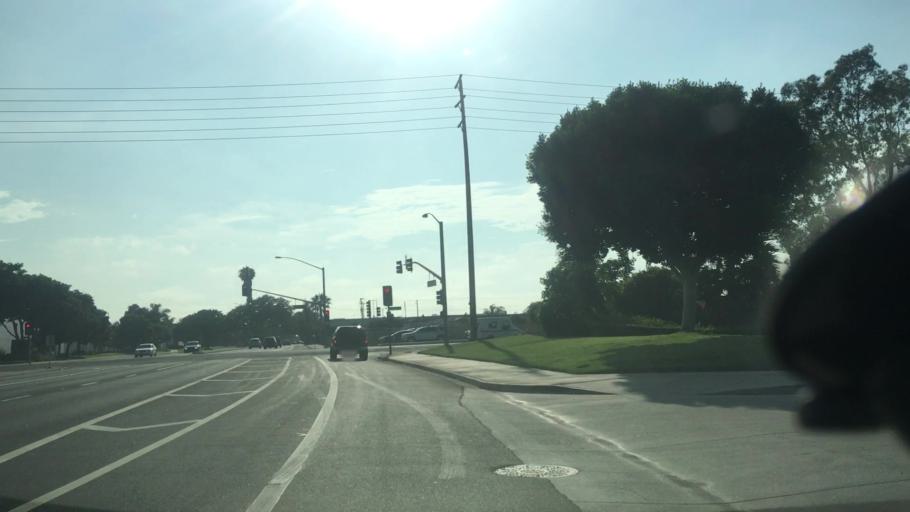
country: US
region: California
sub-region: Ventura County
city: Oxnard
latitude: 34.2063
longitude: -119.1413
